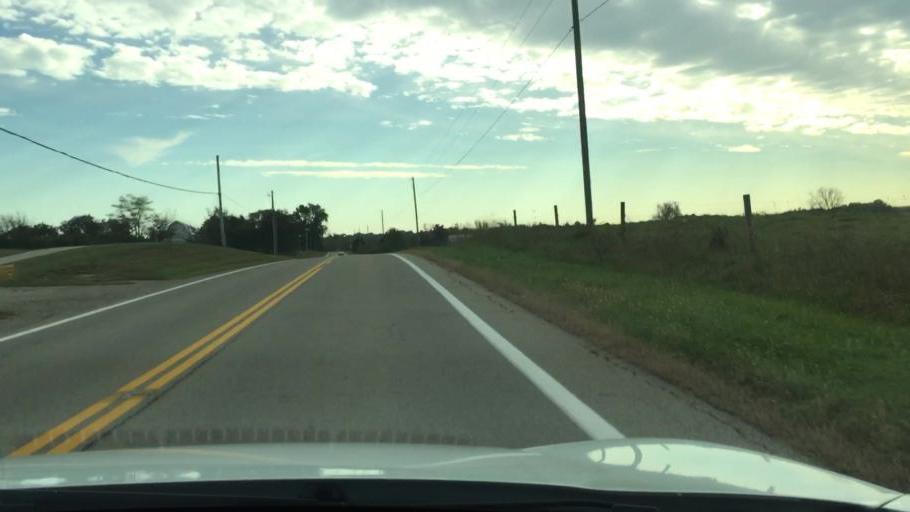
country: US
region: Ohio
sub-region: Champaign County
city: Mechanicsburg
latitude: 40.0968
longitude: -83.5456
